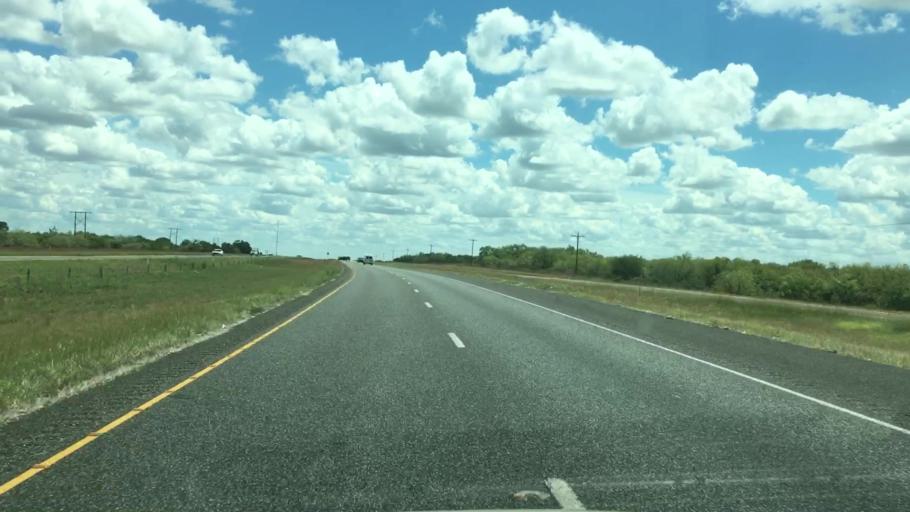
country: US
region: Texas
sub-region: Atascosa County
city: Pleasanton
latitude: 28.8198
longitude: -98.3609
